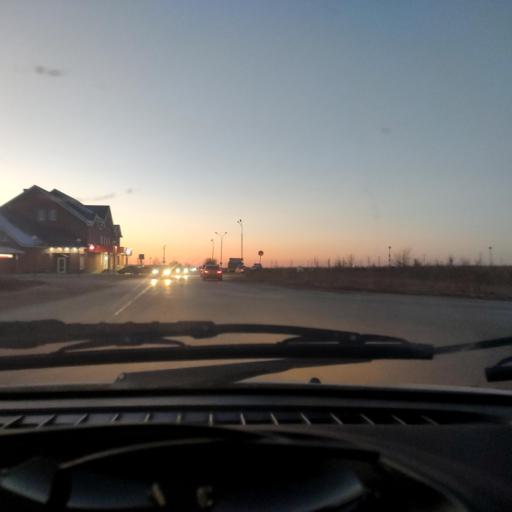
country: RU
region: Samara
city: Podstepki
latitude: 53.5158
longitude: 49.2166
